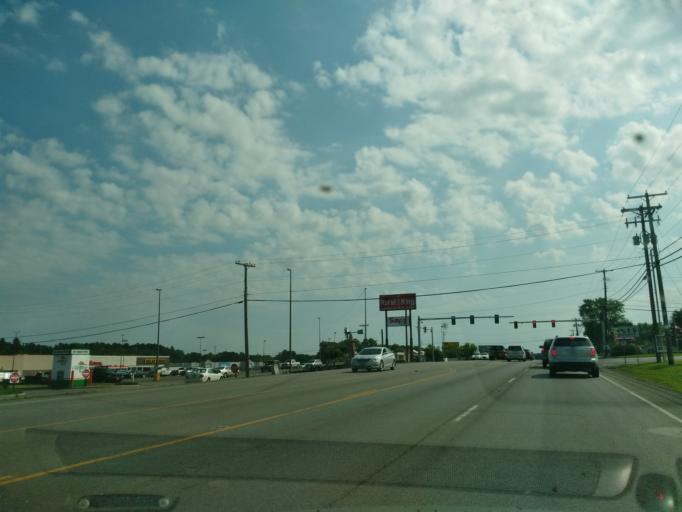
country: US
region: Ohio
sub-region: Muskingum County
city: South Zanesville
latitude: 39.8962
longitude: -82.0401
